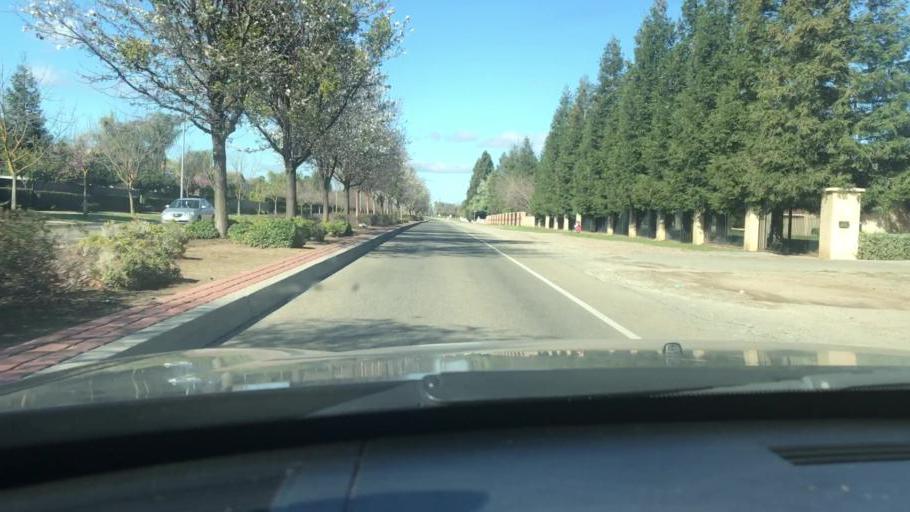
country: US
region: California
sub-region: Fresno County
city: Clovis
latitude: 36.8665
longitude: -119.6771
